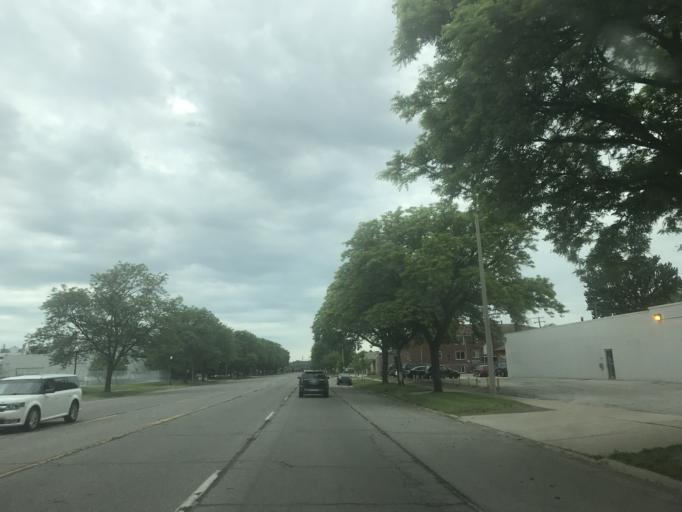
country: US
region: Michigan
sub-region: Wayne County
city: Wyandotte
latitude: 42.2224
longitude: -83.1503
